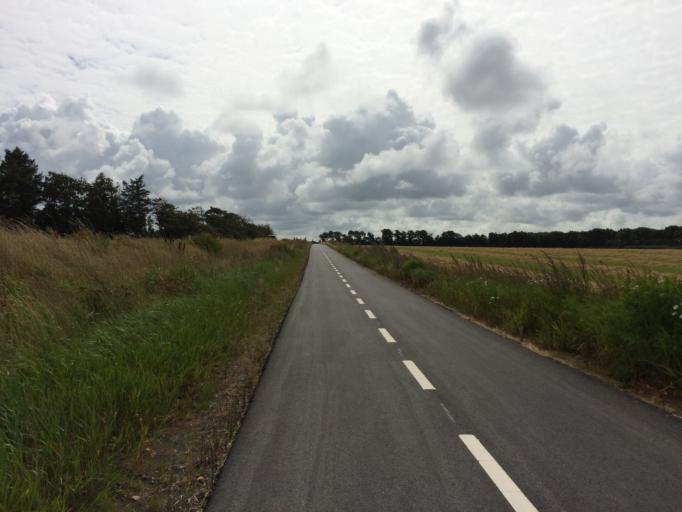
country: DK
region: Central Jutland
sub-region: Holstebro Kommune
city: Ulfborg
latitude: 56.3235
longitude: 8.3420
